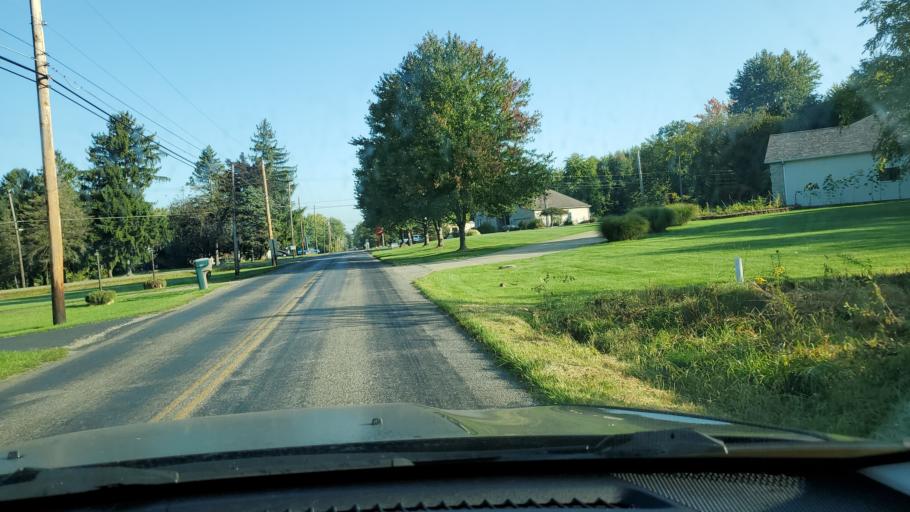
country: US
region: Ohio
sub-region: Trumbull County
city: Mineral Ridge
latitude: 41.1592
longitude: -80.7534
